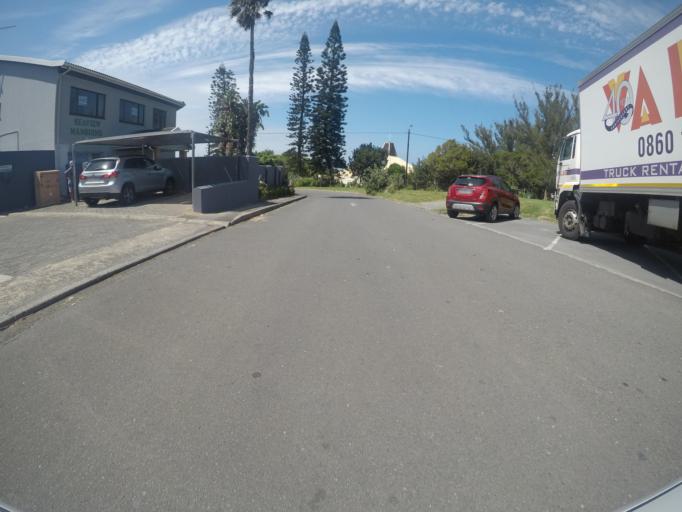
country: ZA
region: Eastern Cape
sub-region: Buffalo City Metropolitan Municipality
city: East London
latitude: -32.9410
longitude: 28.0230
